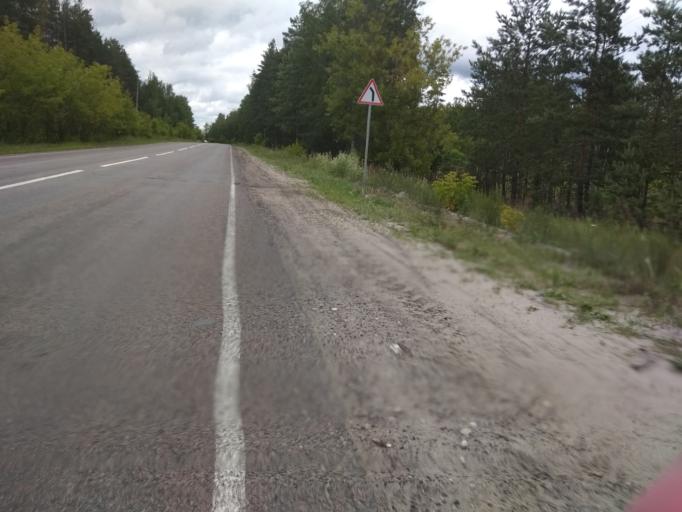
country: RU
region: Moskovskaya
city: Kerva
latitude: 55.5797
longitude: 39.6900
